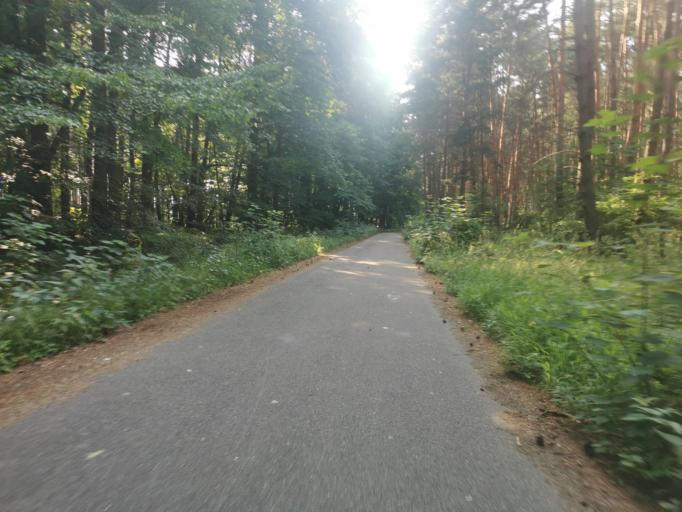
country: CZ
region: South Moravian
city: Ratiskovice
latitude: 48.9214
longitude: 17.2007
